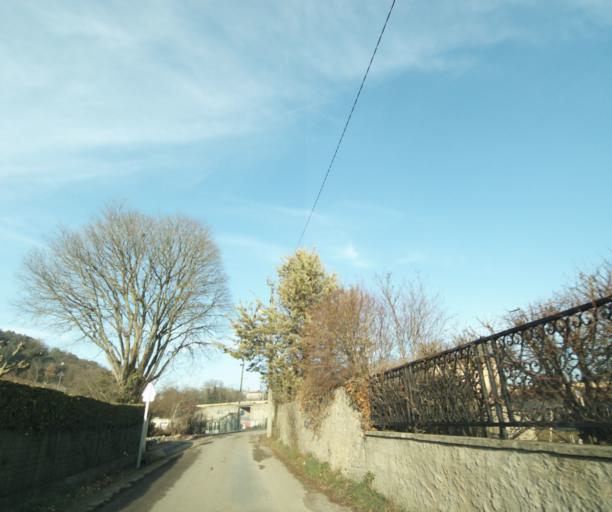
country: FR
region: Provence-Alpes-Cote d'Azur
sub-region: Departement du Var
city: Tourves
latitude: 43.4048
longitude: 5.9253
